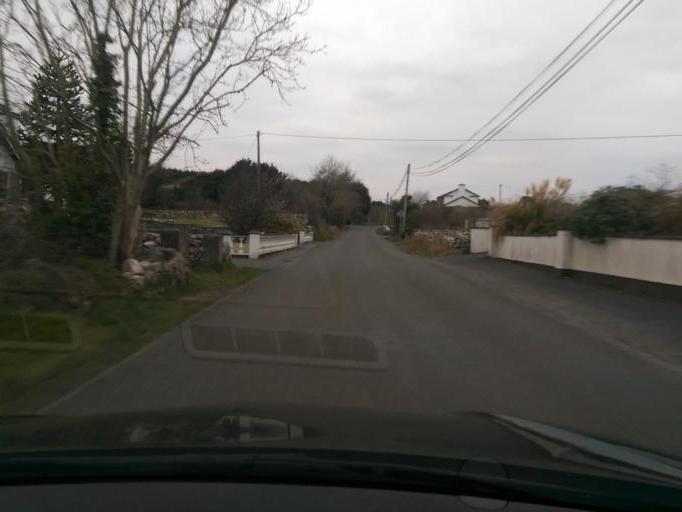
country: IE
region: Connaught
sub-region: County Galway
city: Bearna
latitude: 53.2536
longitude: -9.1533
